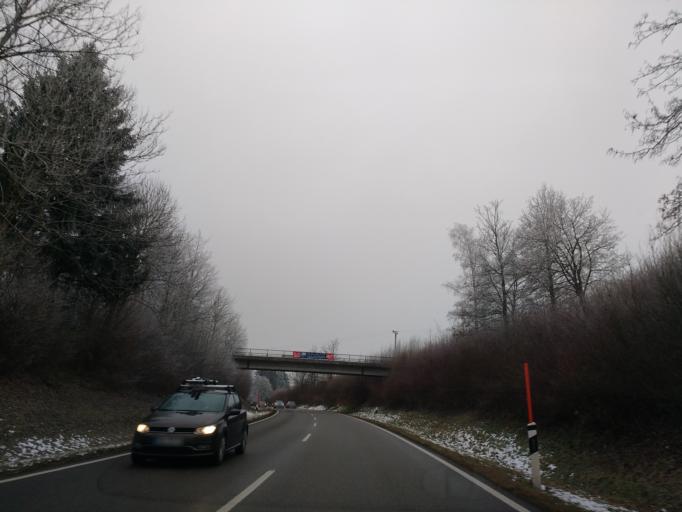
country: DE
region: Bavaria
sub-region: Swabia
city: Oy-Mittelberg
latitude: 47.6495
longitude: 10.4634
